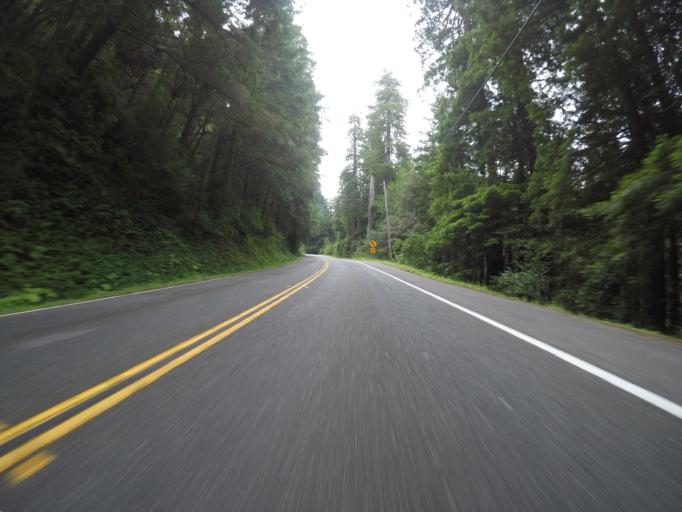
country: US
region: California
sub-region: Humboldt County
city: Rio Dell
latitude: 40.4057
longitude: -123.9525
